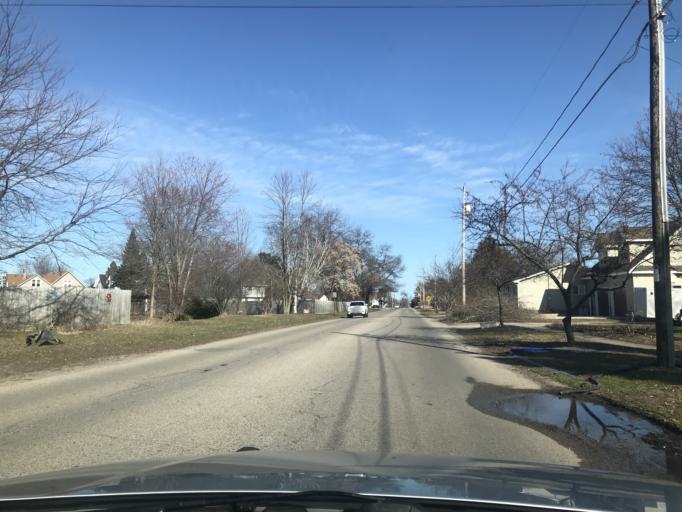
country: US
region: Wisconsin
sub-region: Marinette County
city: Marinette
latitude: 45.0926
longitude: -87.6451
